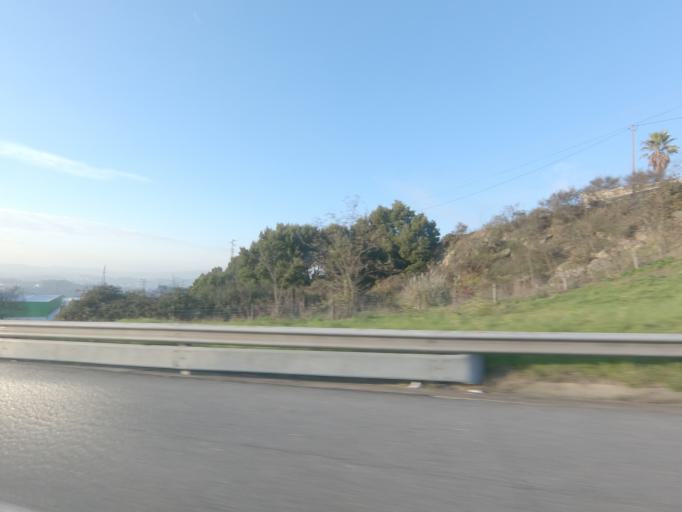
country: PT
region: Porto
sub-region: Penafiel
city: Penafiel
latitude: 41.2139
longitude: -8.2829
